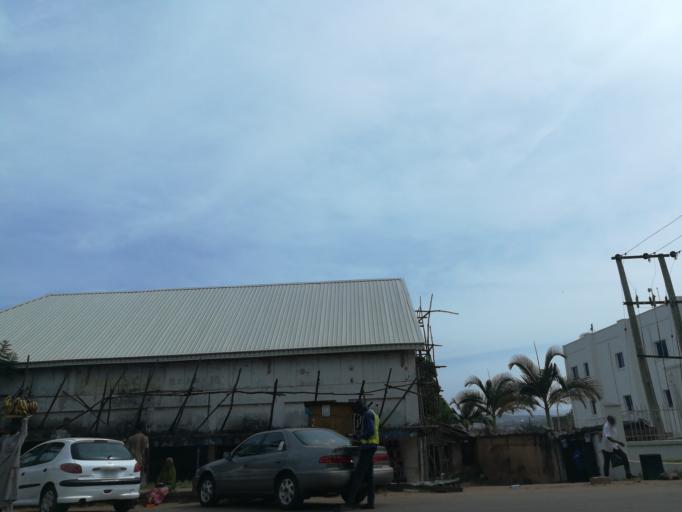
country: NG
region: Plateau
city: Jos
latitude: 9.9128
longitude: 8.8905
